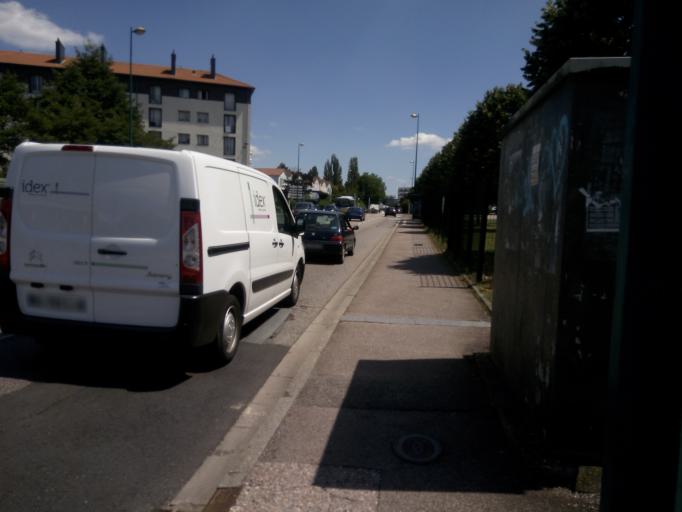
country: FR
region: Lorraine
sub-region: Departement de Meurthe-et-Moselle
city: Villers-les-Nancy
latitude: 48.6687
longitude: 6.1612
